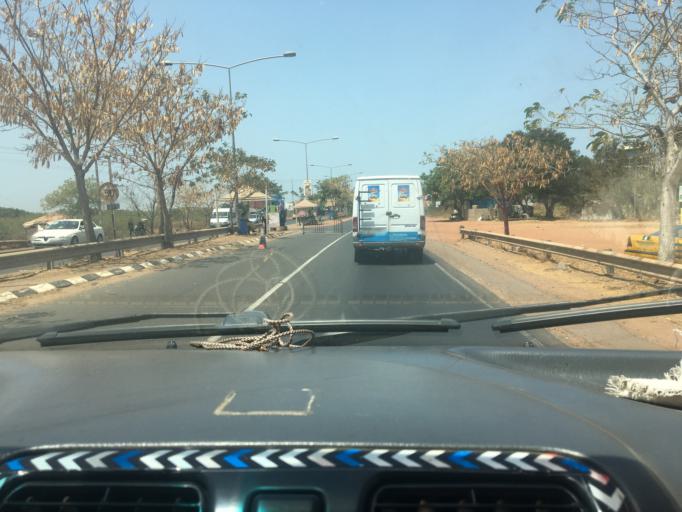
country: GM
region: Banjul
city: Bakau
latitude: 13.4681
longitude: -16.6296
